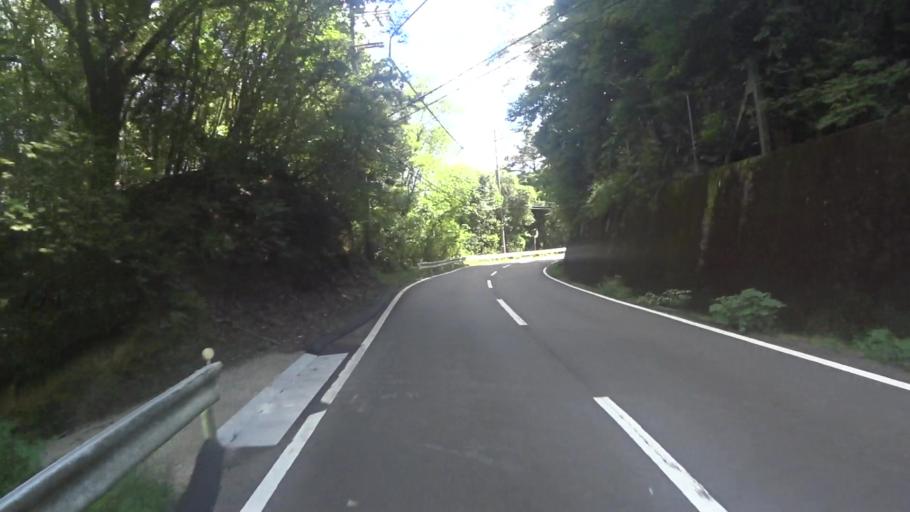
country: JP
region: Mie
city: Ueno-ebisumachi
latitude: 34.7389
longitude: 136.0000
